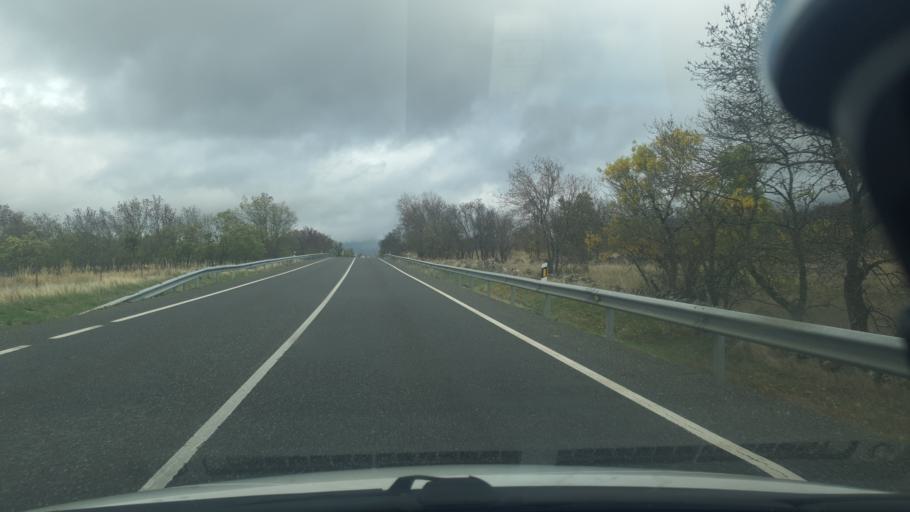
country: ES
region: Castille and Leon
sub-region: Provincia de Segovia
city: Sotosalbos
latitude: 41.0257
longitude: -3.9498
